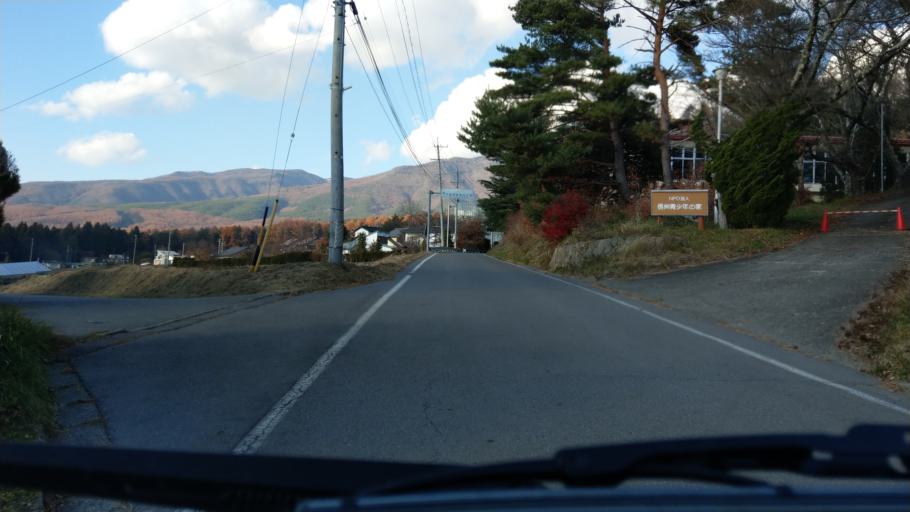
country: JP
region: Nagano
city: Komoro
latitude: 36.3511
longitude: 138.4582
